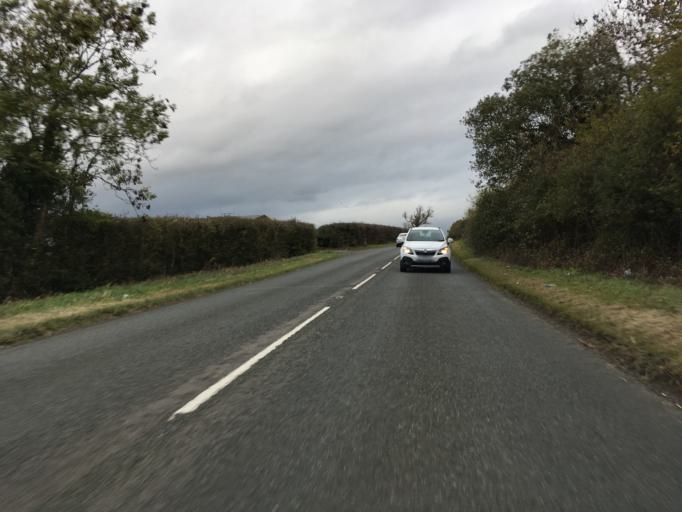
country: GB
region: England
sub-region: South Gloucestershire
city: Pucklechurch
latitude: 51.5078
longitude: -2.4273
